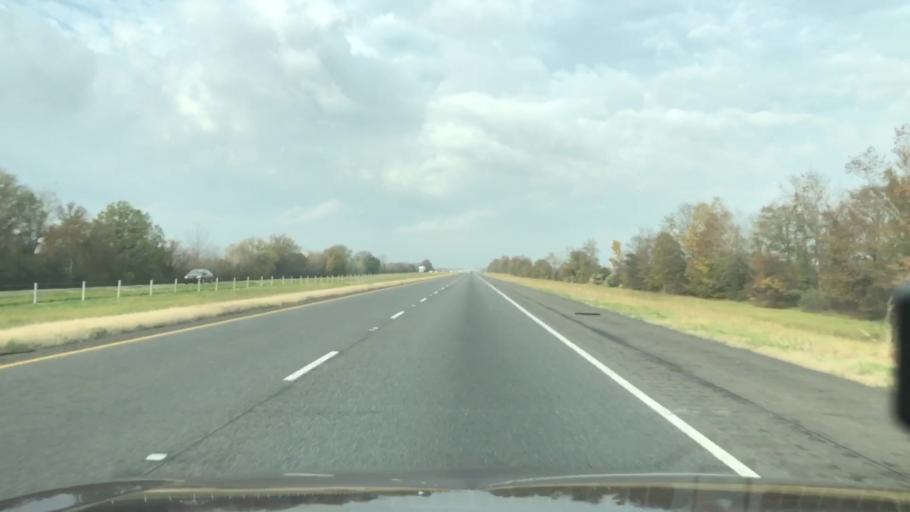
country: US
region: Louisiana
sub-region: Richland Parish
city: Delhi
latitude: 32.4271
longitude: -91.3897
